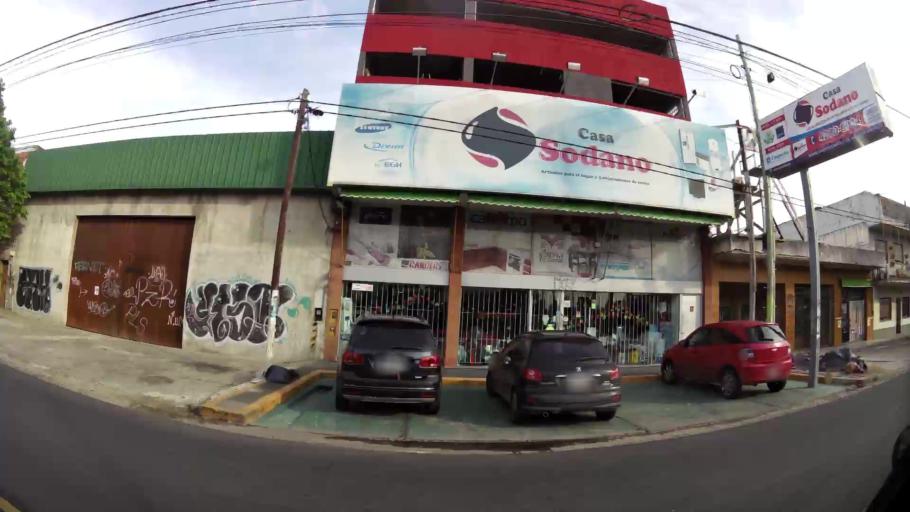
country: AR
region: Buenos Aires
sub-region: Partido de Quilmes
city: Quilmes
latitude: -34.7405
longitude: -58.2673
